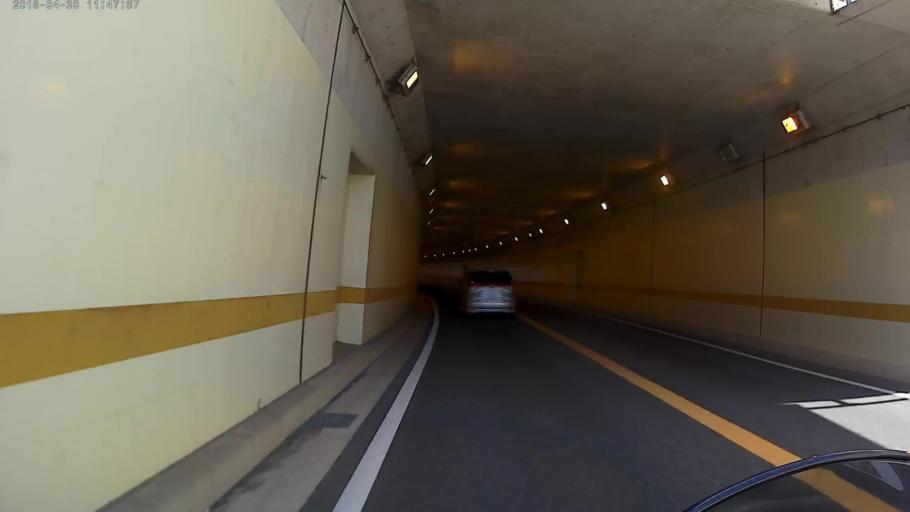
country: JP
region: Kanagawa
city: Zama
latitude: 35.4867
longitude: 139.3658
